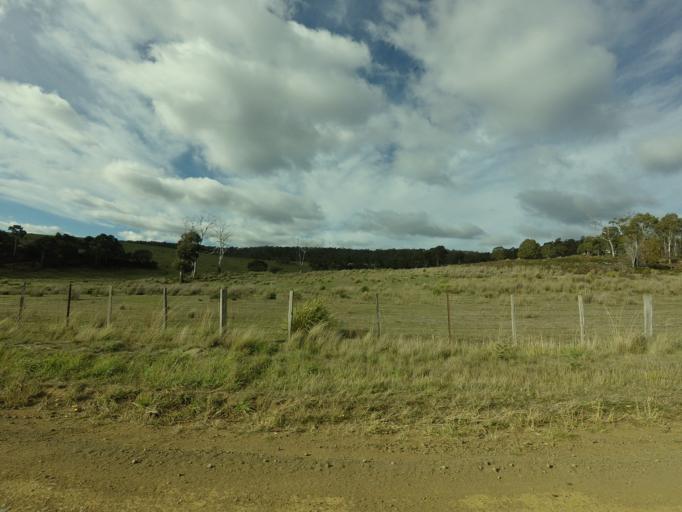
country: AU
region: Tasmania
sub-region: Brighton
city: Bridgewater
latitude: -42.4766
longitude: 147.2924
